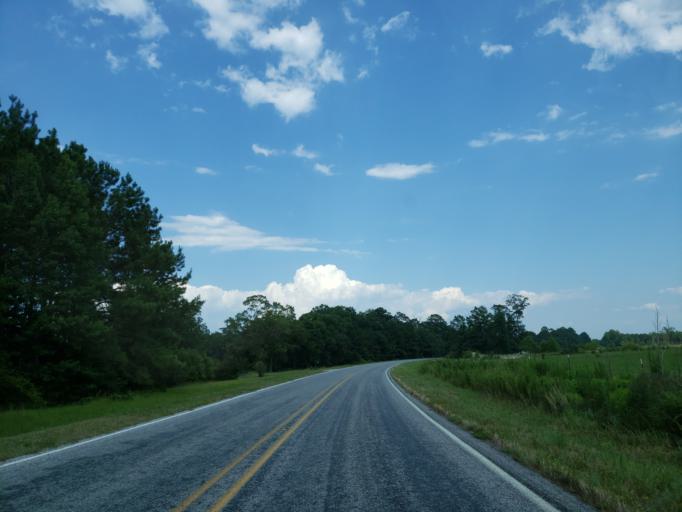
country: US
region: Mississippi
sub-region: Jones County
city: Ellisville
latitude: 31.6236
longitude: -89.3619
